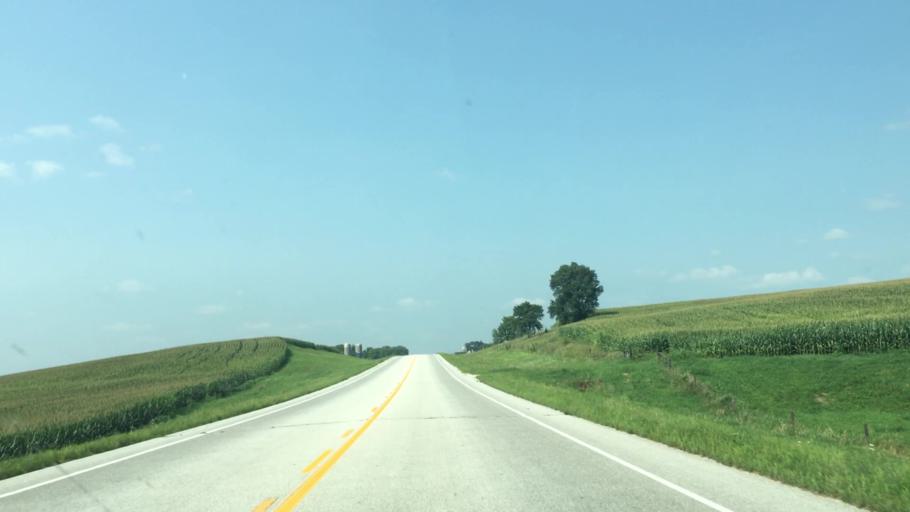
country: US
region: Minnesota
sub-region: Fillmore County
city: Harmony
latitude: 43.6067
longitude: -91.9297
